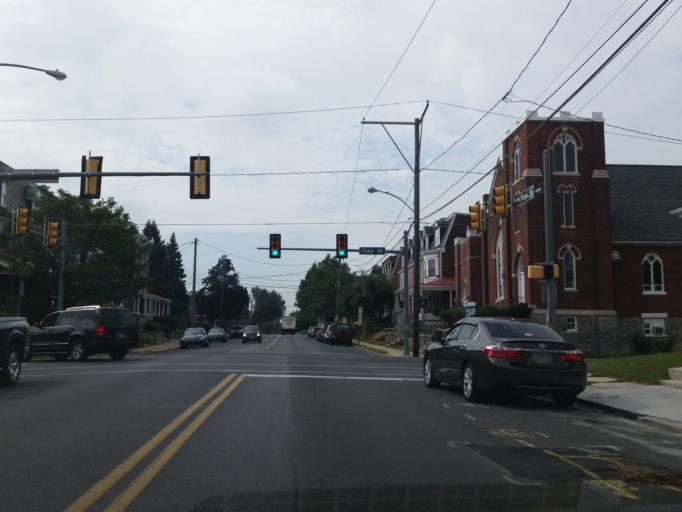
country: US
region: Pennsylvania
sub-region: Lancaster County
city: Lancaster
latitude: 40.0510
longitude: -76.2993
